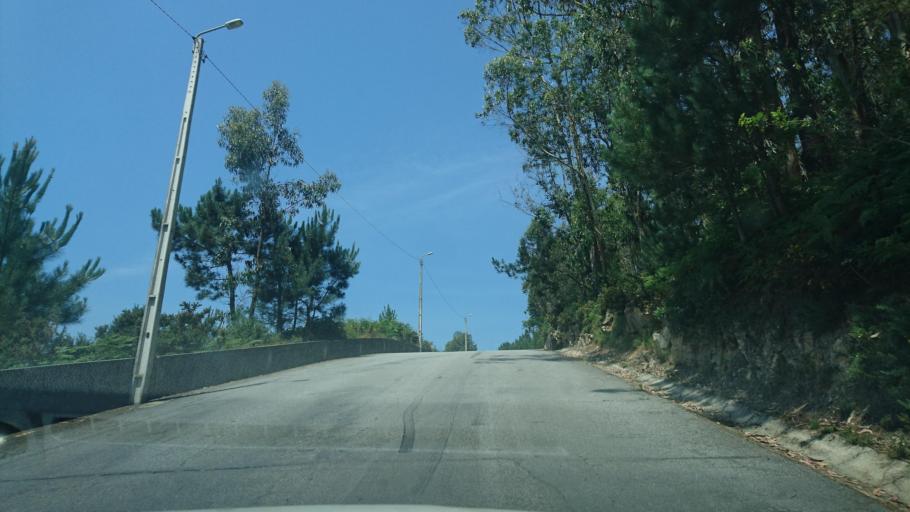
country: PT
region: Porto
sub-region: Matosinhos
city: Lavra
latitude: 41.2708
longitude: -8.7211
